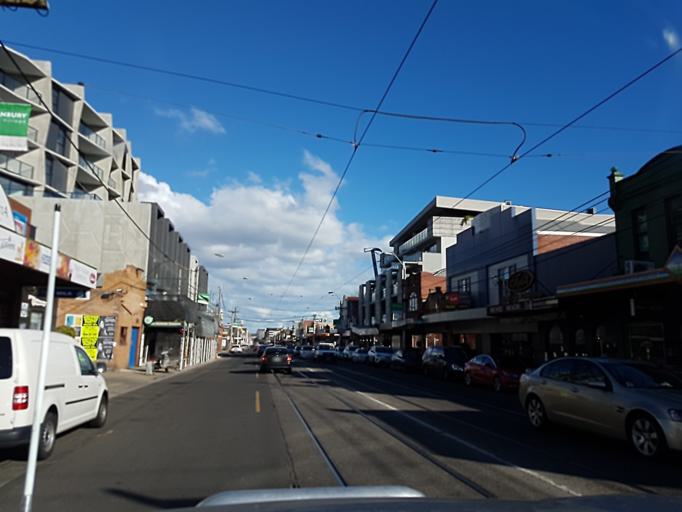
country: AU
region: Victoria
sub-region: Darebin
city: Thornbury
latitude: -37.7597
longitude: 145.0005
